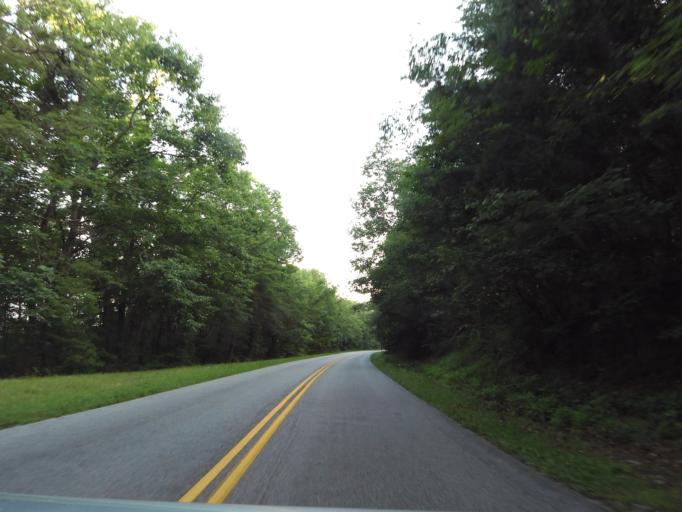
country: US
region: Tennessee
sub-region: Blount County
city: Maryville
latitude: 35.6345
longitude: -83.9385
